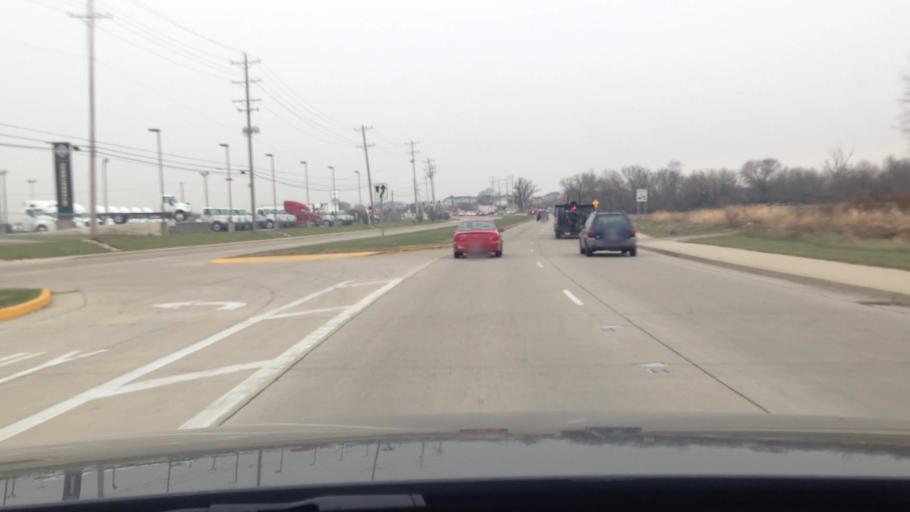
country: US
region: Illinois
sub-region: McHenry County
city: Huntley
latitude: 42.1578
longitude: -88.4301
